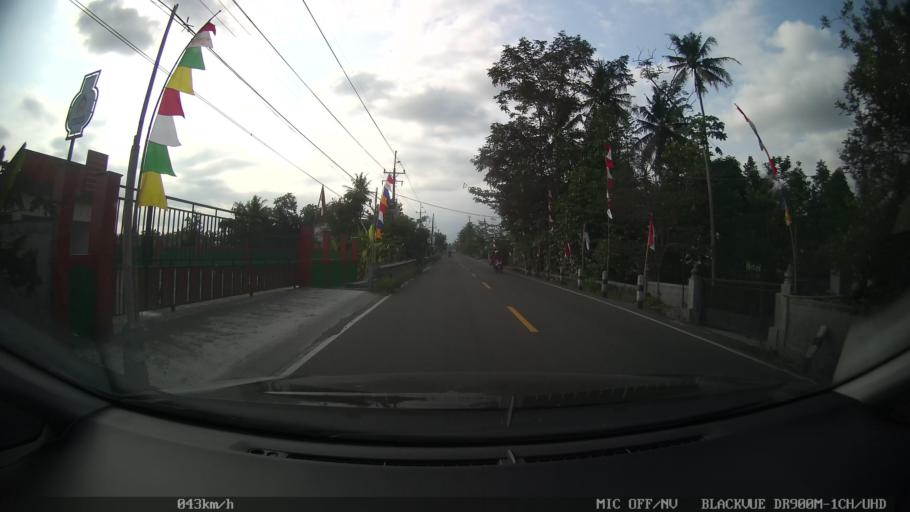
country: ID
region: Central Java
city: Candi Prambanan
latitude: -7.7050
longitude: 110.4678
